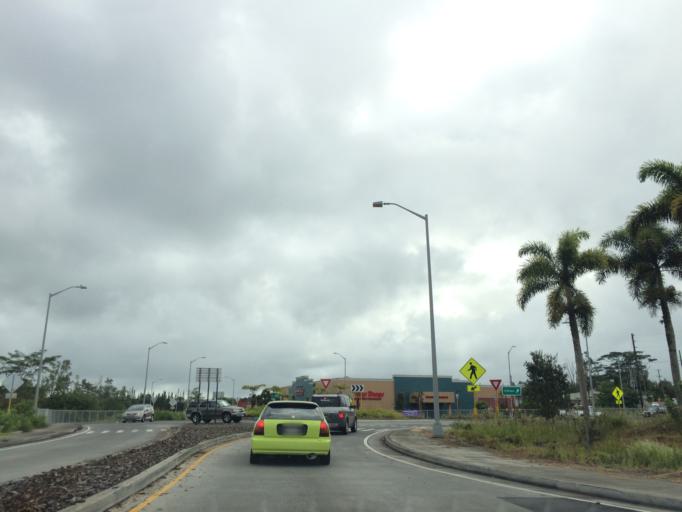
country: US
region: Hawaii
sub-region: Hawaii County
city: Hawaiian Paradise Park
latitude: 19.5056
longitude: -154.9566
